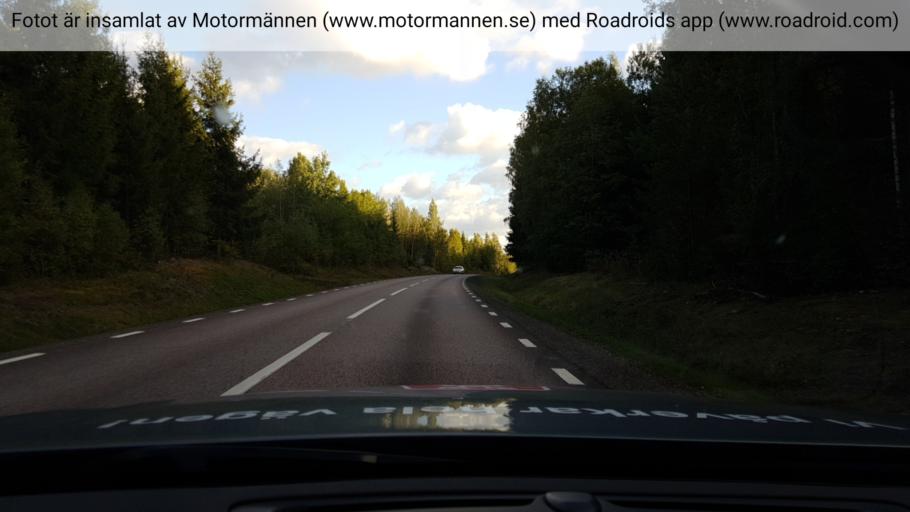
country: SE
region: Vaermland
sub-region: Karlstads Kommun
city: Molkom
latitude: 59.6450
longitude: 13.7147
